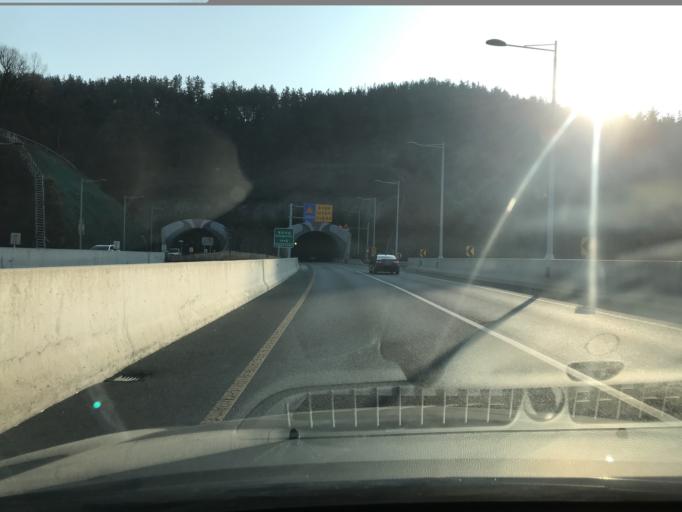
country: KR
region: Daegu
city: Hwawon
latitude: 35.7974
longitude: 128.5104
